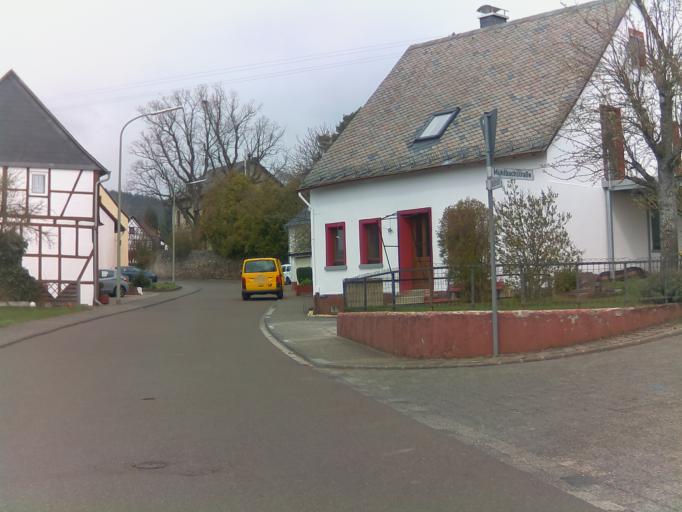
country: DE
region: Rheinland-Pfalz
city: Schauren
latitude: 49.8061
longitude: 7.2407
